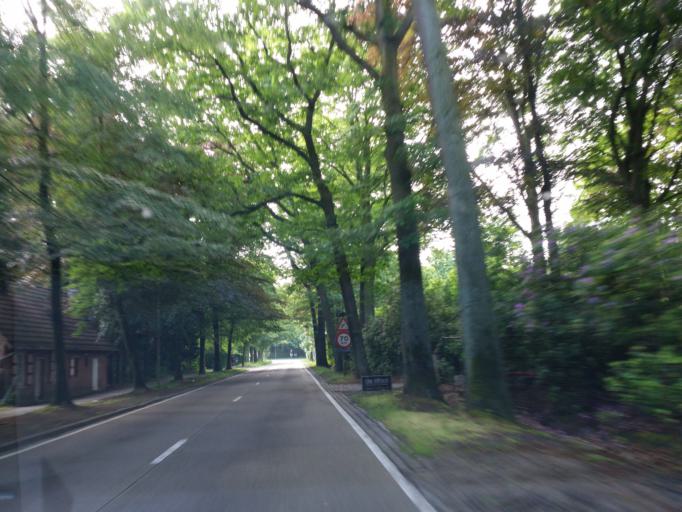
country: BE
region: Flanders
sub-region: Provincie Antwerpen
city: Brasschaat
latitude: 51.3146
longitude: 4.4731
